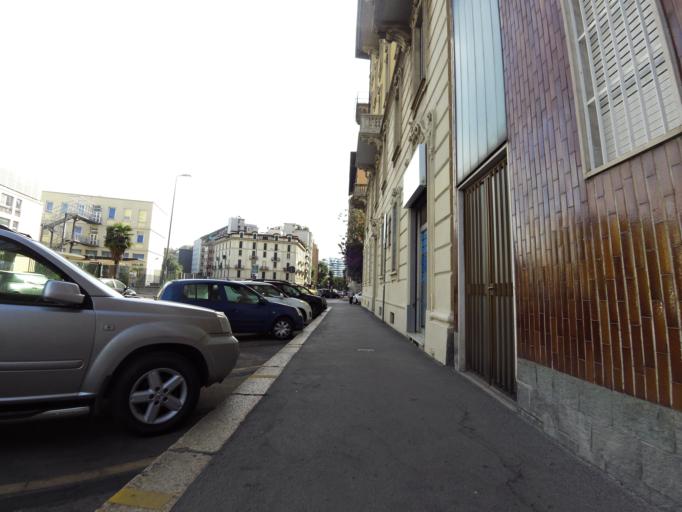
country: IT
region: Lombardy
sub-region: Citta metropolitana di Milano
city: Milano
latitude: 45.4792
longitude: 9.1637
